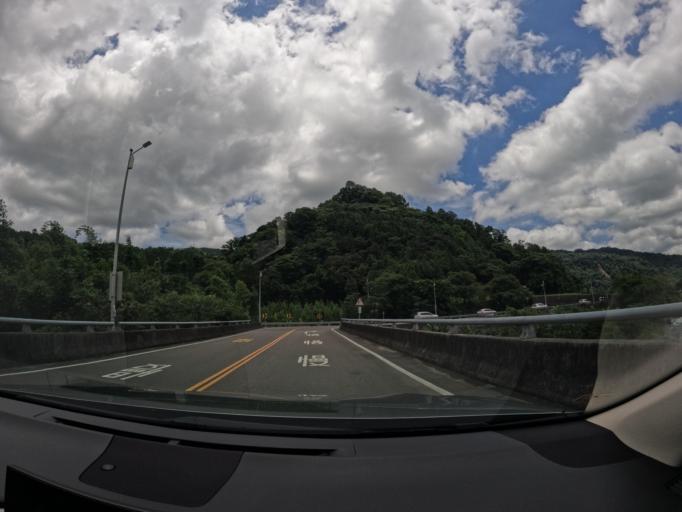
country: TW
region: Taiwan
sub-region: Miaoli
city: Miaoli
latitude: 24.5934
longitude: 120.9991
